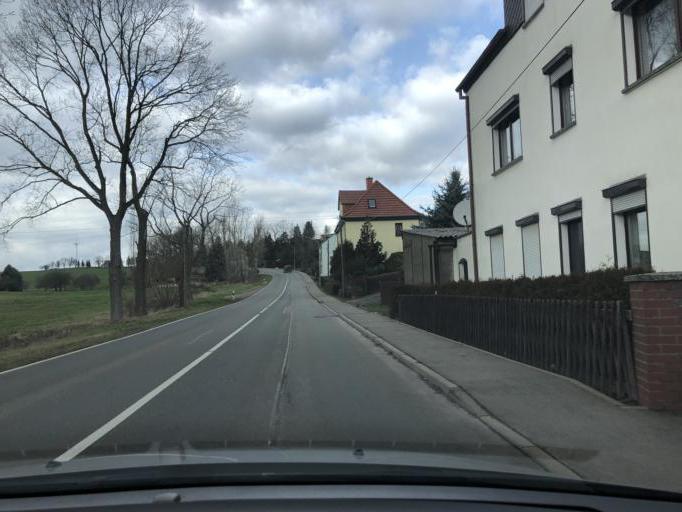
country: DE
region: Saxony
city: Dobeln
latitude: 51.1427
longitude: 13.0931
